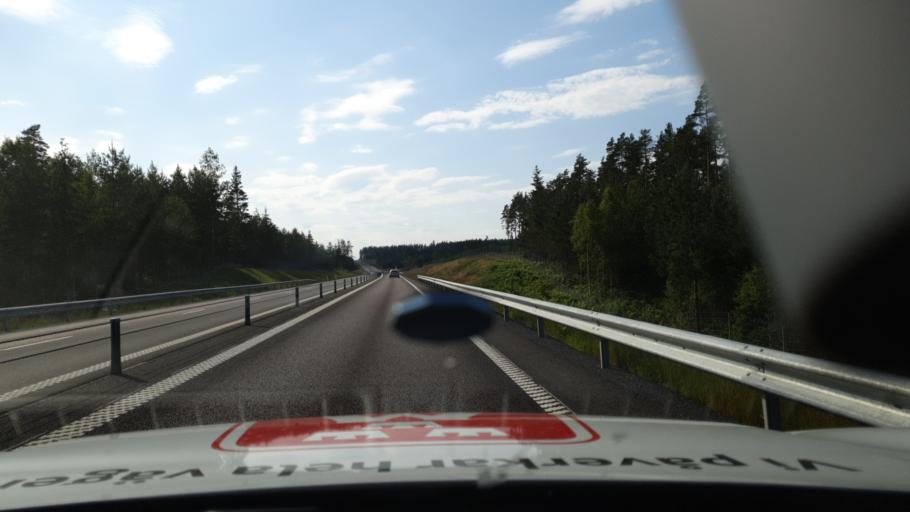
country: SE
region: Joenkoeping
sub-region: Mullsjo Kommun
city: Mullsjoe
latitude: 57.8694
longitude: 13.9588
